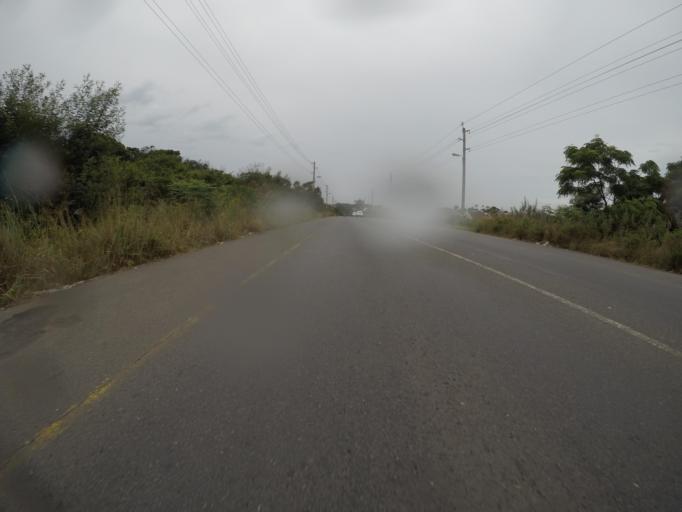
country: ZA
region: Eastern Cape
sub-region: Buffalo City Metropolitan Municipality
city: East London
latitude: -32.9975
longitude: 27.8381
